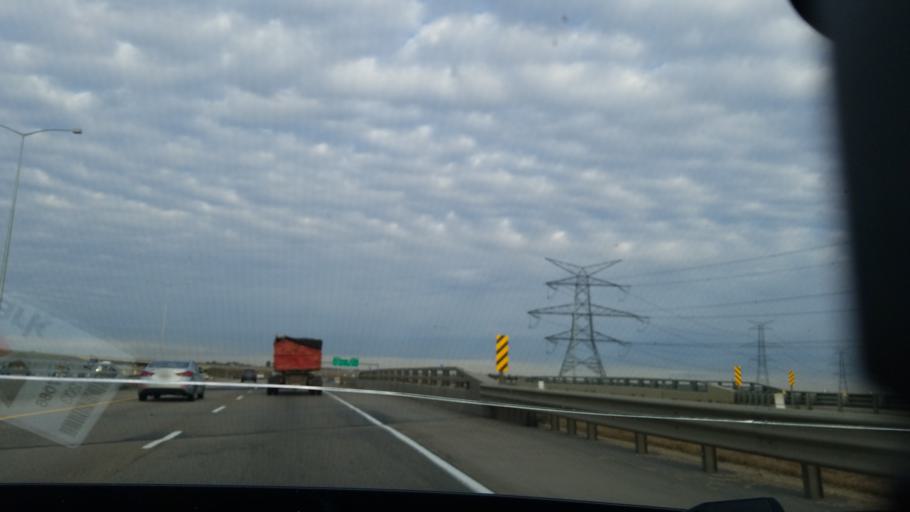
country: CA
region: Alberta
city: Edmonton
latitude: 53.6306
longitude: -113.3807
